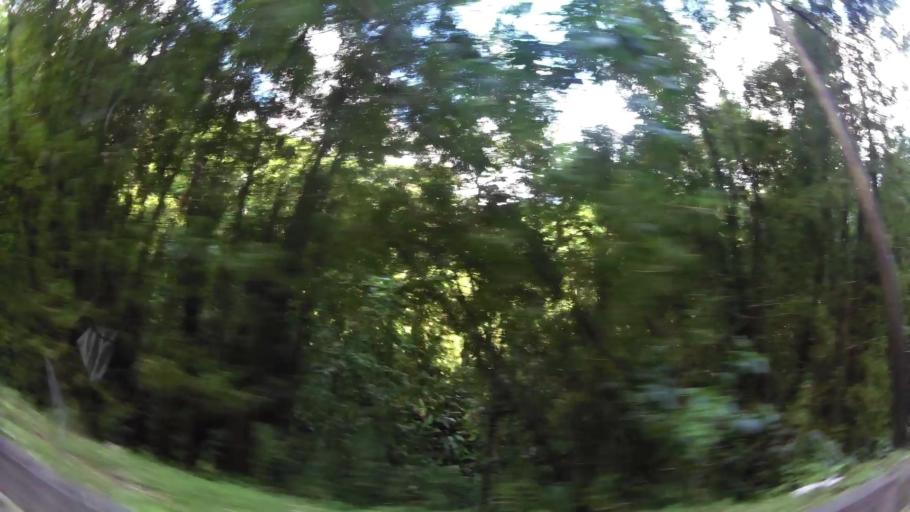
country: MQ
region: Martinique
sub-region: Martinique
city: Saint-Joseph
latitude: 14.6915
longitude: -61.0883
